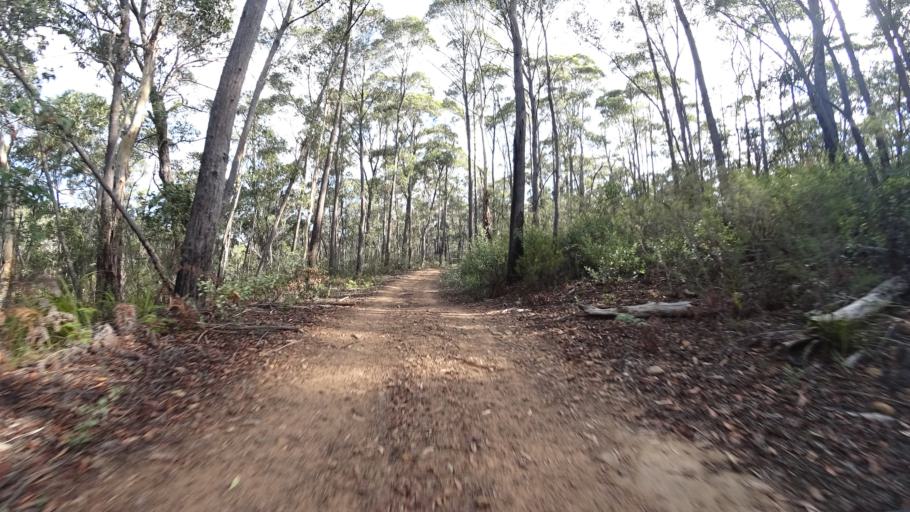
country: AU
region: New South Wales
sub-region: Lithgow
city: Lithgow
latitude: -33.3325
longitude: 150.2890
